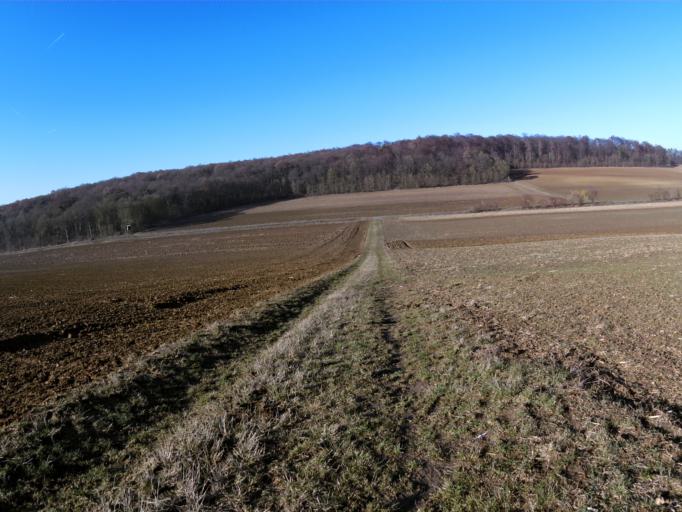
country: DE
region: Bavaria
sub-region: Regierungsbezirk Unterfranken
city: Estenfeld
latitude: 49.8483
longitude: 9.9942
